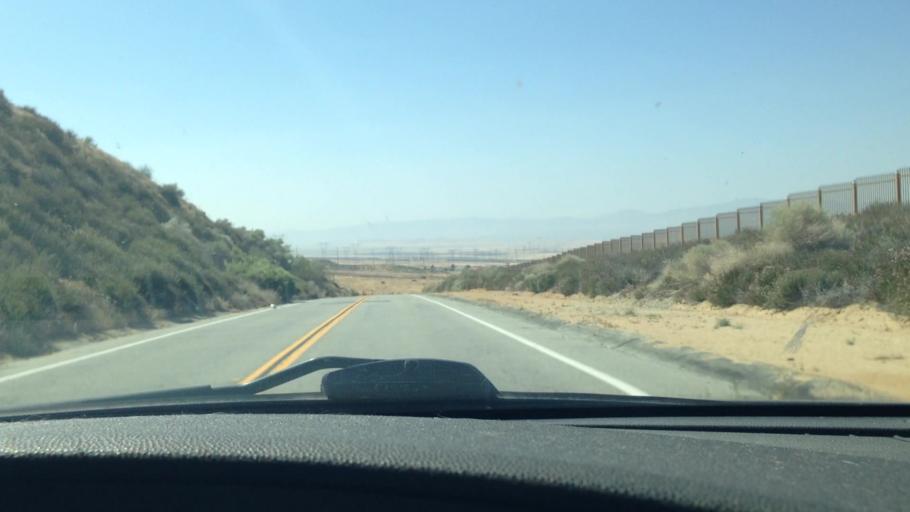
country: US
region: California
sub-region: Los Angeles County
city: Quartz Hill
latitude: 34.6324
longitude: -118.2506
